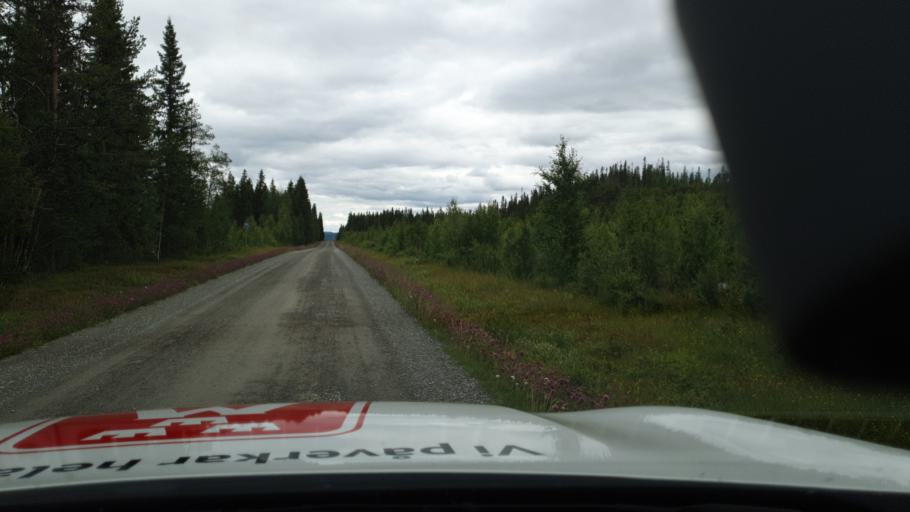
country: SE
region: Vaesterbotten
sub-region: Storumans Kommun
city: Storuman
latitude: 64.7716
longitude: 17.0439
